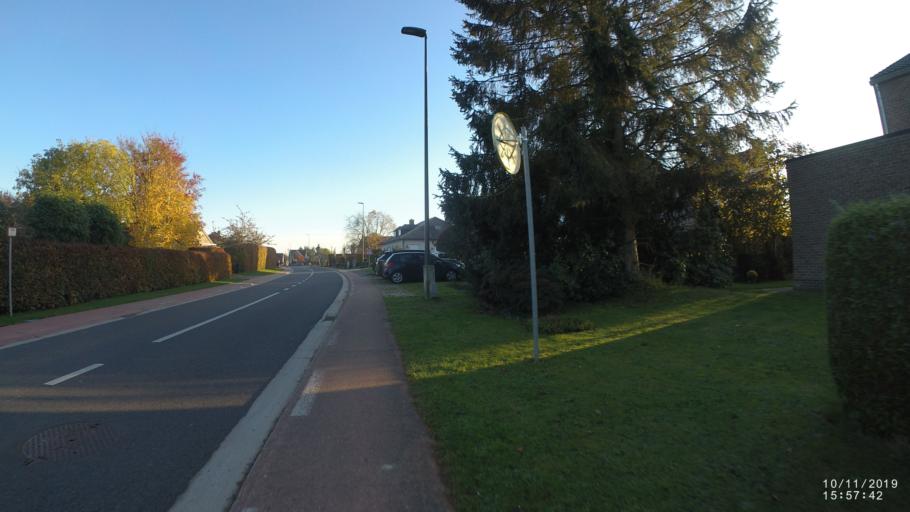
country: BE
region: Flanders
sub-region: Provincie Vlaams-Brabant
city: Lubbeek
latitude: 50.9026
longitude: 4.8865
